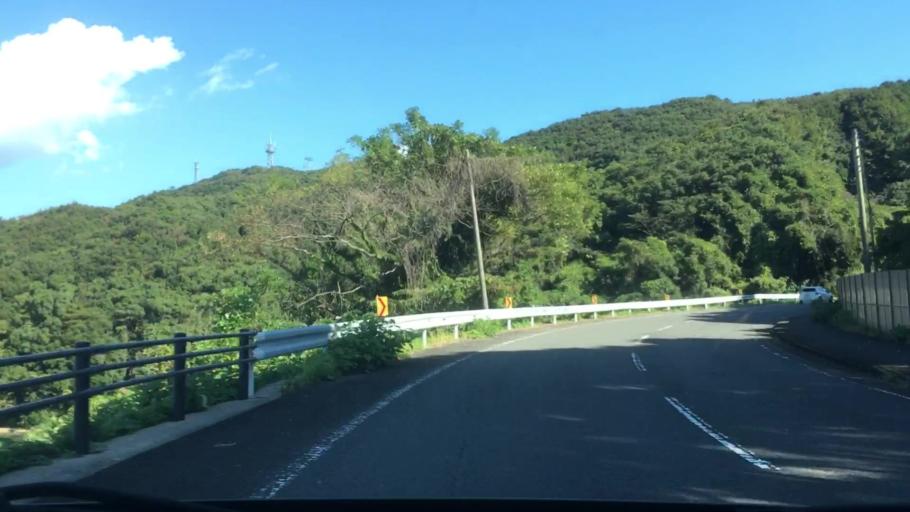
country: JP
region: Nagasaki
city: Sasebo
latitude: 32.9901
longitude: 129.6476
